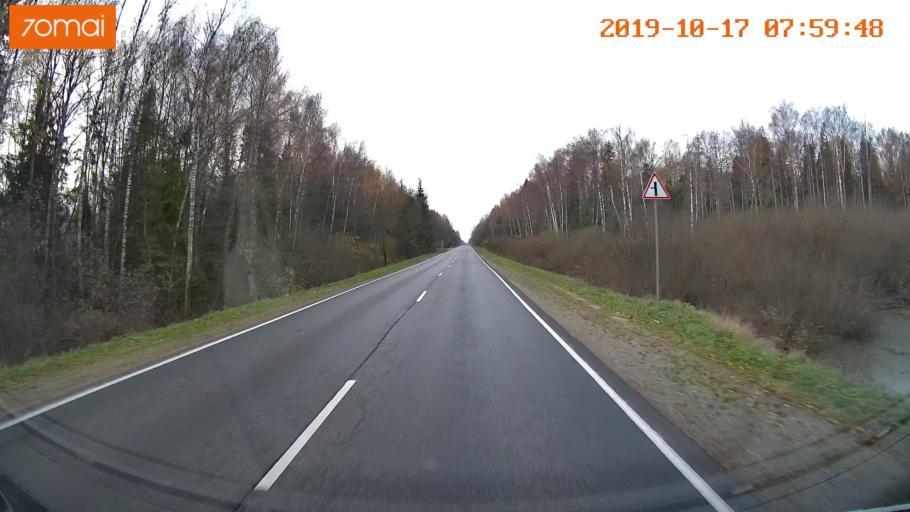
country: RU
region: Vladimir
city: Bavleny
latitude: 56.3898
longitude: 39.5312
